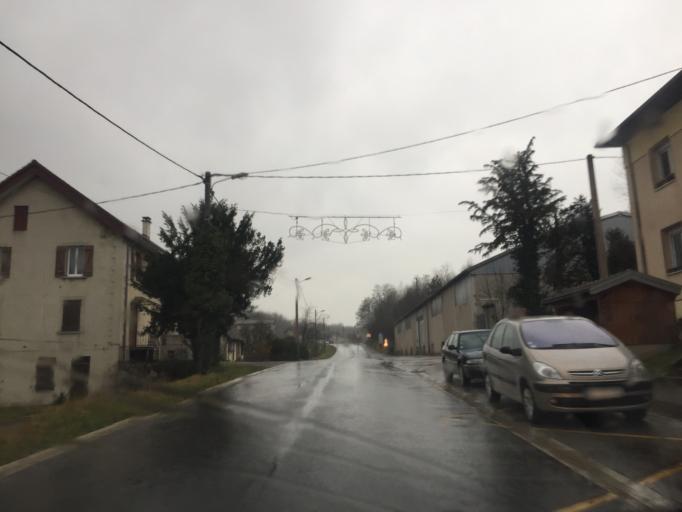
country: FR
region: Franche-Comte
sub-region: Departement du Jura
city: Mouchard
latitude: 46.9796
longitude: 5.8095
